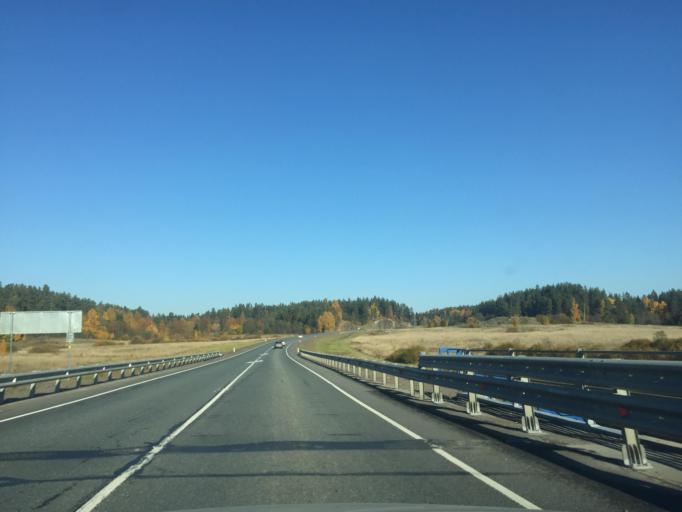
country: RU
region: Leningrad
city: Kuznechnoye
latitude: 61.3049
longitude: 29.7850
